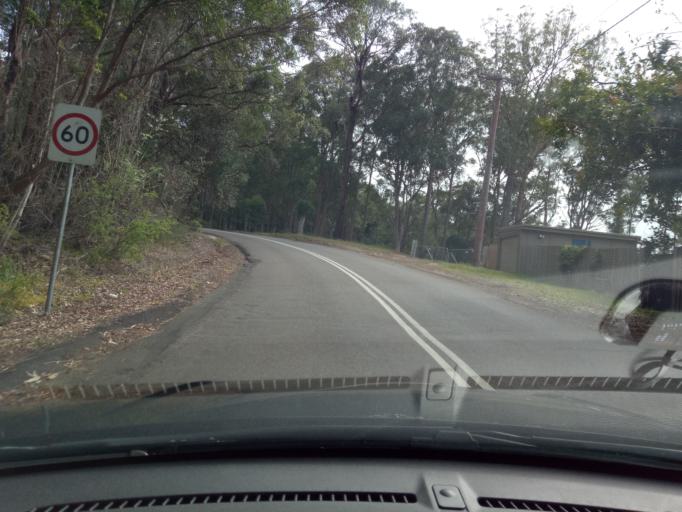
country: AU
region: New South Wales
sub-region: Gosford Shire
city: Holgate
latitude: -33.3956
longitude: 151.4034
